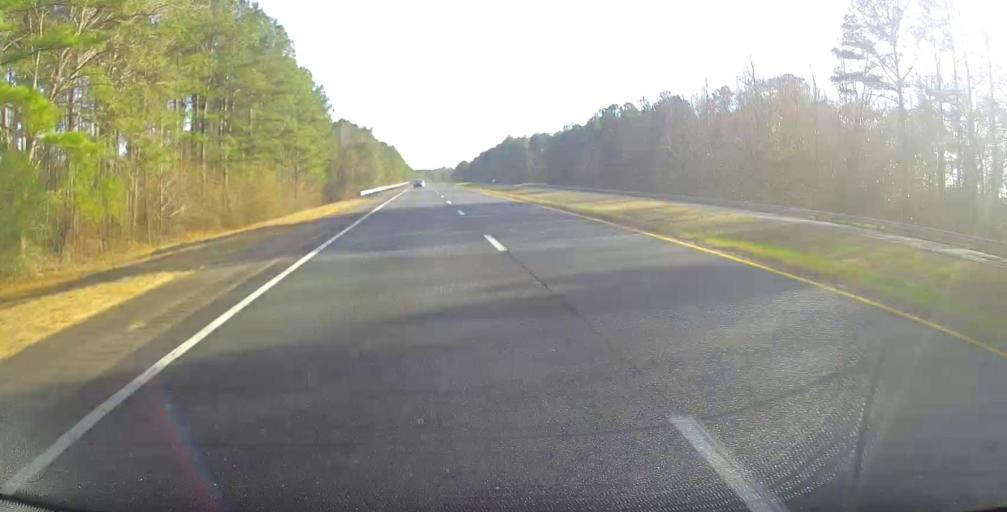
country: US
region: Georgia
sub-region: Harris County
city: Hamilton
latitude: 32.5873
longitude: -84.8206
